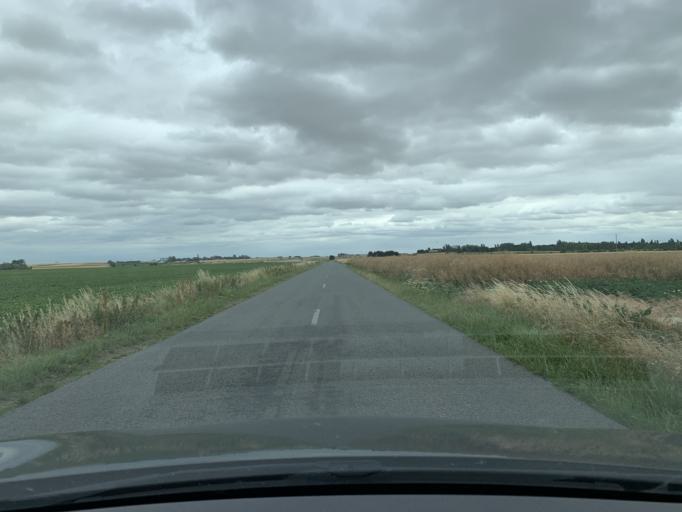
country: FR
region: Nord-Pas-de-Calais
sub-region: Departement du Pas-de-Calais
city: Oisy-le-Verger
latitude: 50.2209
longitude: 3.1218
